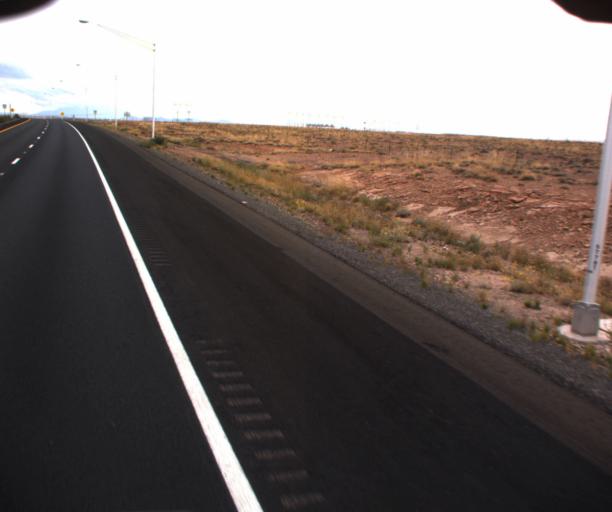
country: US
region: Arizona
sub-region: Coconino County
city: Tuba City
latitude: 35.8418
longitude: -111.4352
